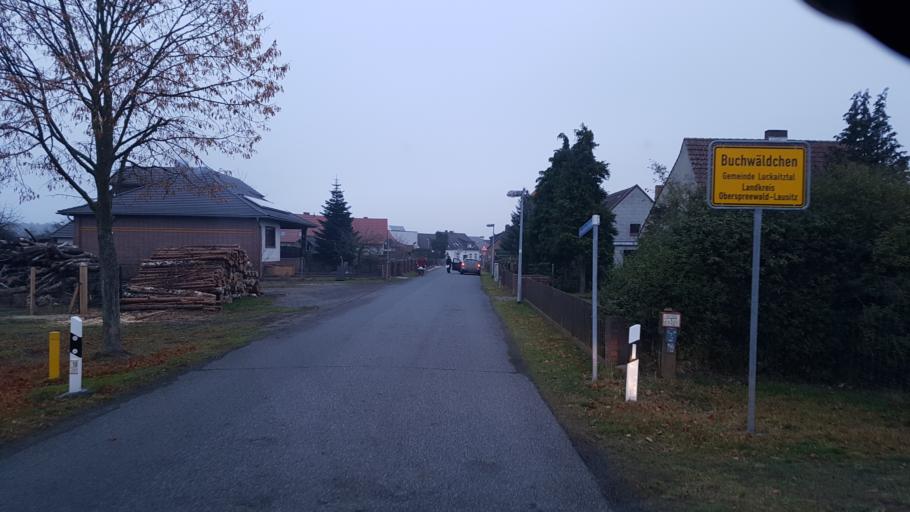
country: DE
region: Brandenburg
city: Altdobern
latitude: 51.6926
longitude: 14.0037
